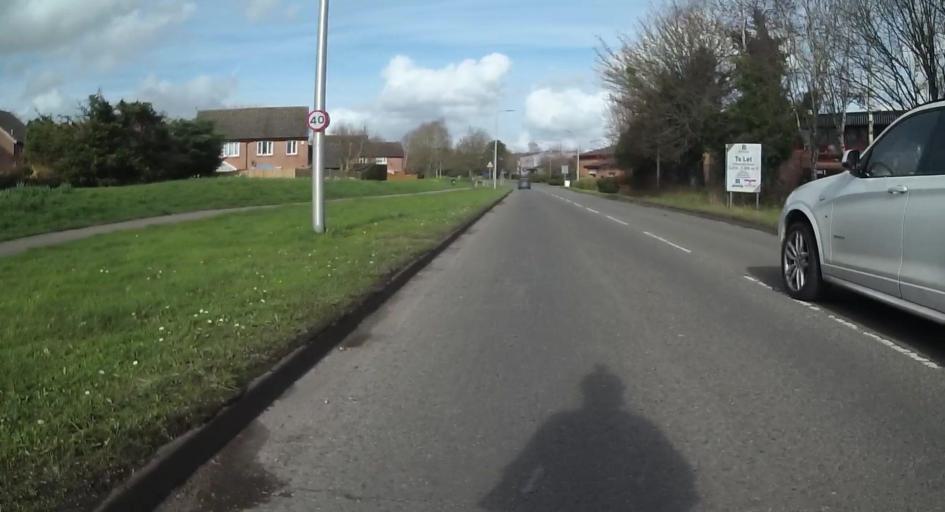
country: GB
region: England
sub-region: West Berkshire
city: Thatcham
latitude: 51.3977
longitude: -1.2390
